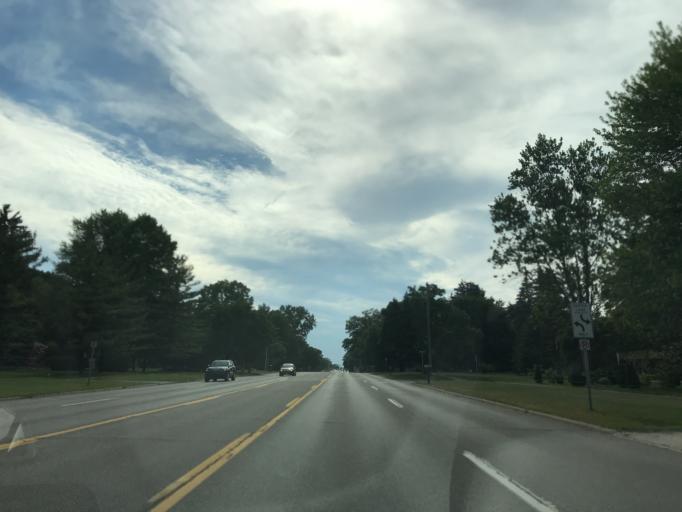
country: US
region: Michigan
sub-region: Wayne County
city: Livonia
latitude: 42.4120
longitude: -83.3648
